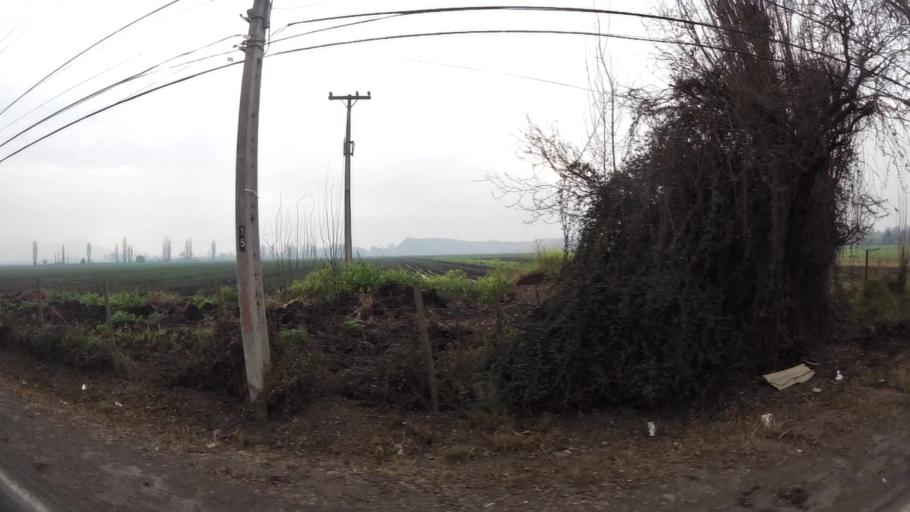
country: CL
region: Santiago Metropolitan
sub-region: Provincia de Chacabuco
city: Chicureo Abajo
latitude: -33.2513
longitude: -70.7634
